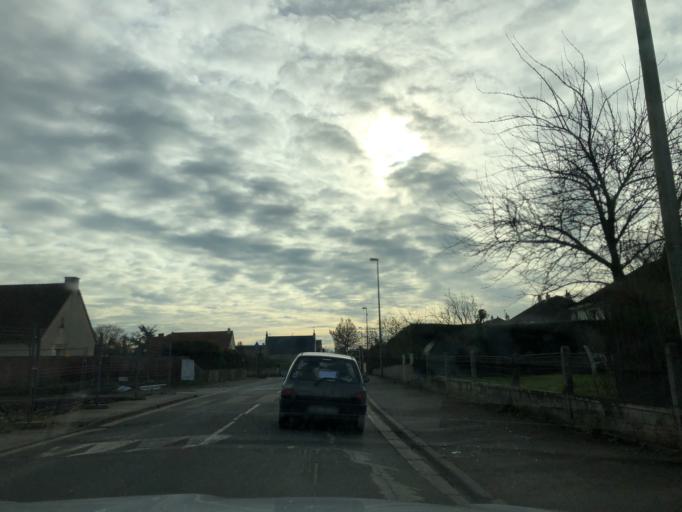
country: FR
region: Lower Normandy
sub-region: Departement du Calvados
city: Beuville
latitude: 49.2469
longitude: -0.3303
